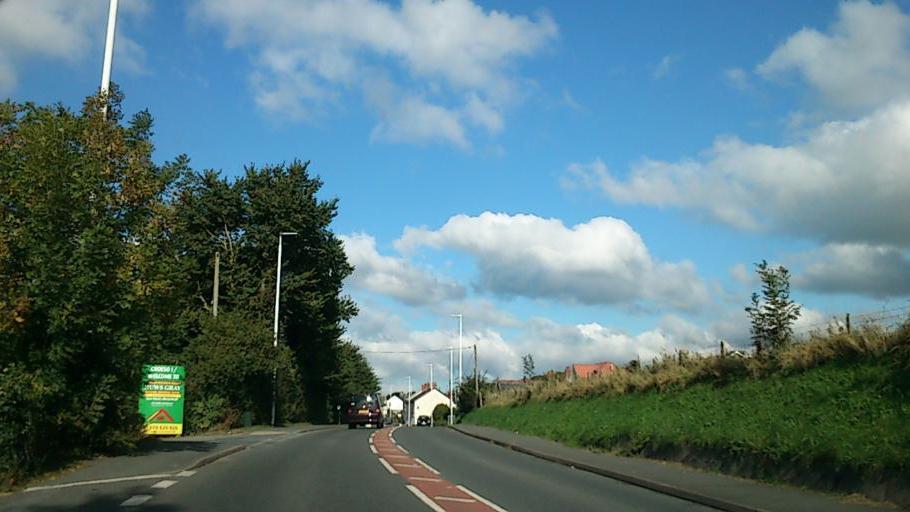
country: GB
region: Wales
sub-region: County of Ceredigion
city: Bow Street
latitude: 52.4396
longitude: -4.0291
